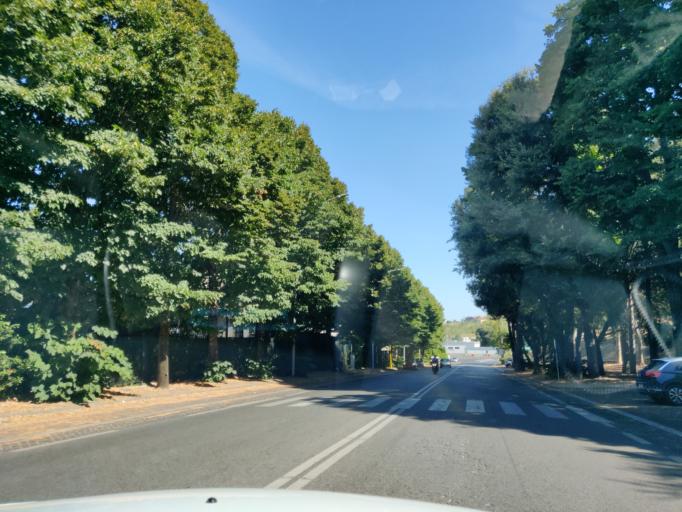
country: IT
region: Latium
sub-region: Citta metropolitana di Roma Capitale
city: Rome
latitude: 41.8363
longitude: 12.4771
